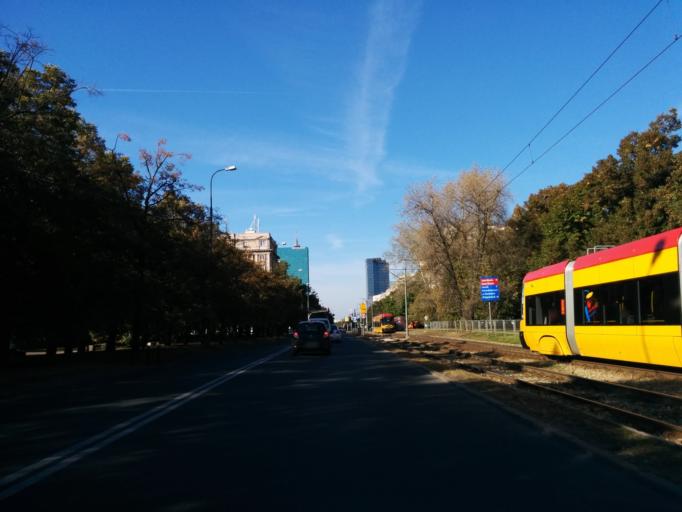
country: PL
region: Masovian Voivodeship
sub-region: Warszawa
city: Wola
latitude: 52.2478
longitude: 20.9991
